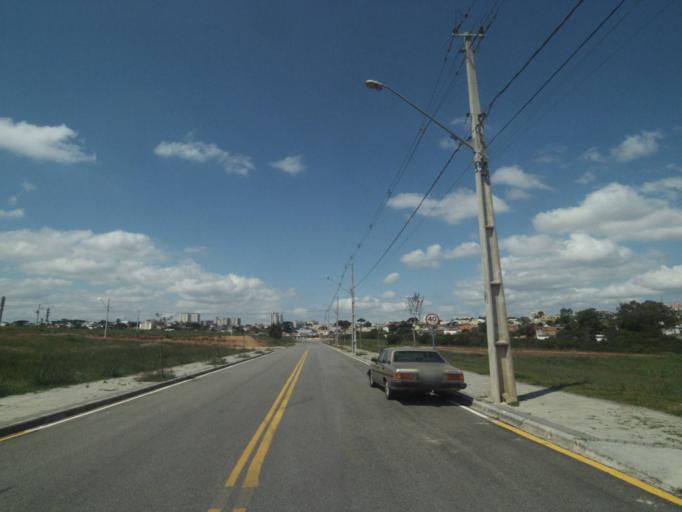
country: BR
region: Parana
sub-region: Curitiba
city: Curitiba
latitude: -25.5097
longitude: -49.3092
